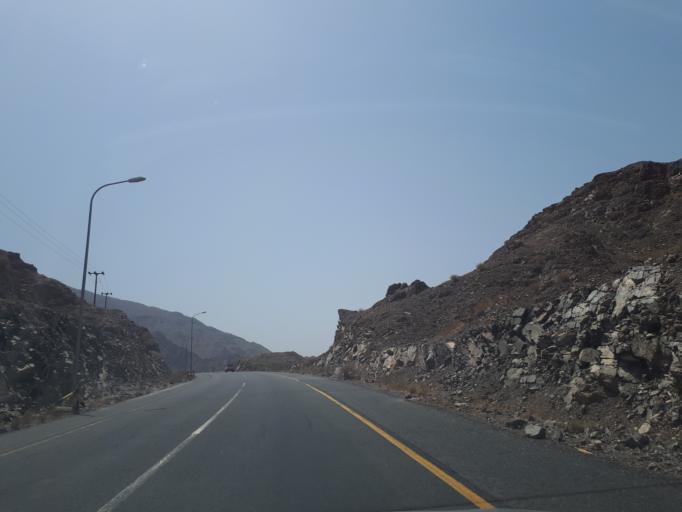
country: OM
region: Muhafazat ad Dakhiliyah
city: Sufalat Sama'il
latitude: 23.1890
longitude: 58.0904
